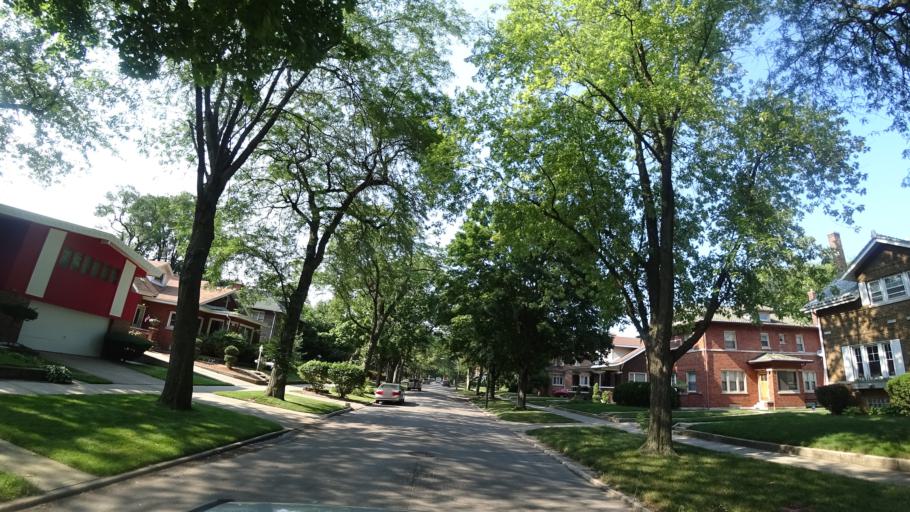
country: US
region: Illinois
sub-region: Cook County
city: Chicago
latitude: 41.7708
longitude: -87.5813
